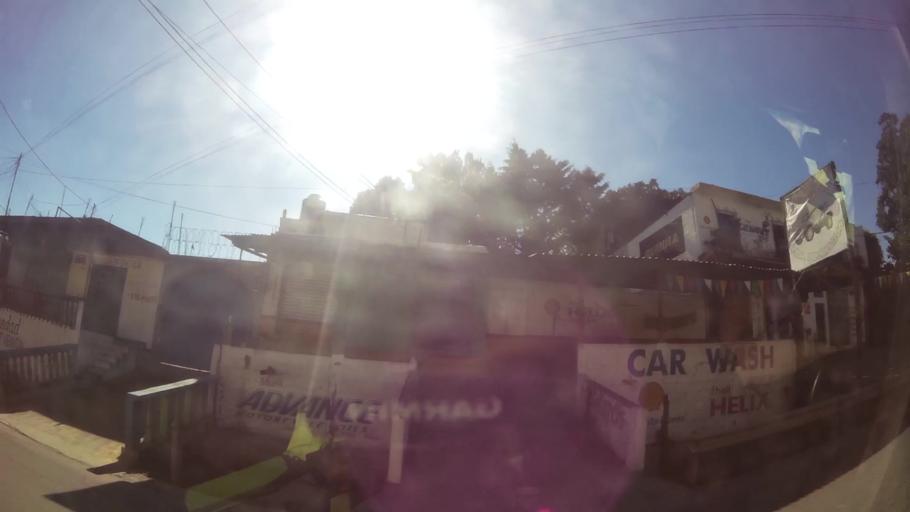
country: GT
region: Guatemala
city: Villa Nueva
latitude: 14.5461
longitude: -90.6182
